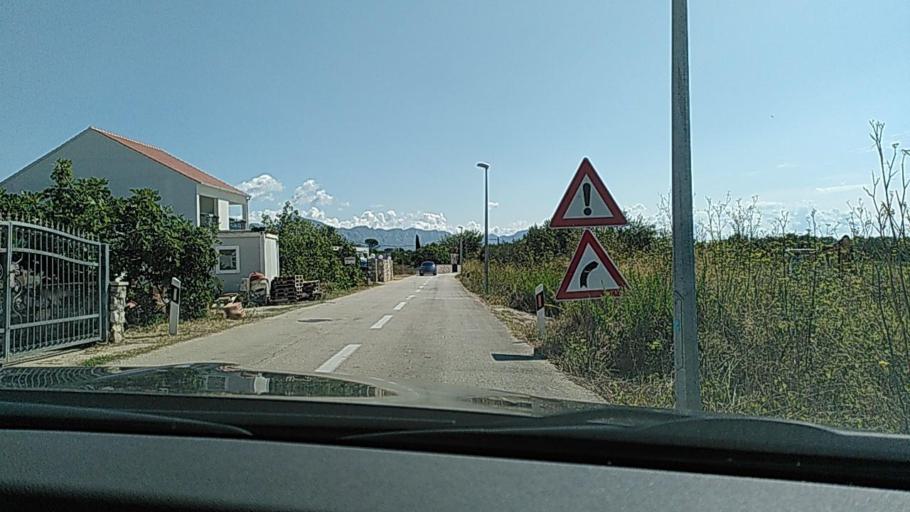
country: HR
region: Dubrovacko-Neretvanska
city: Orebic
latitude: 43.1281
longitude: 17.1811
